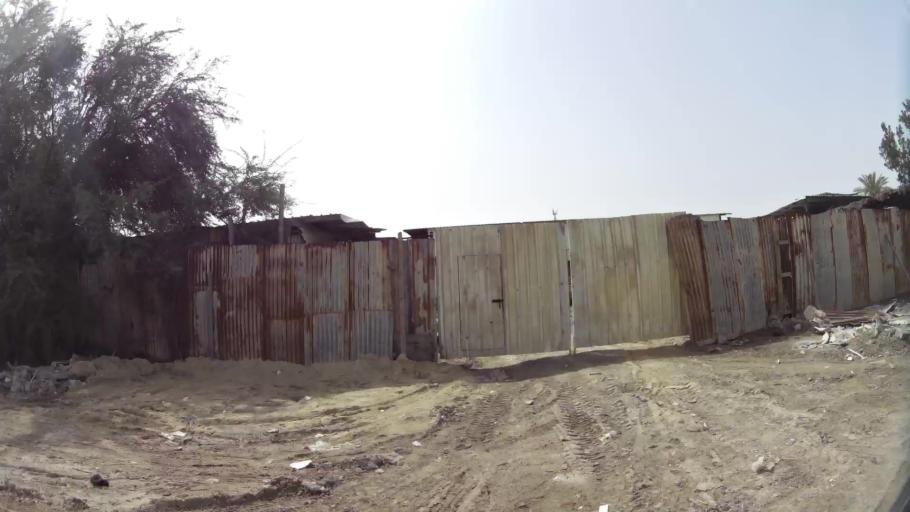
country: BH
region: Manama
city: Jidd Hafs
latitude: 26.2224
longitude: 50.5179
